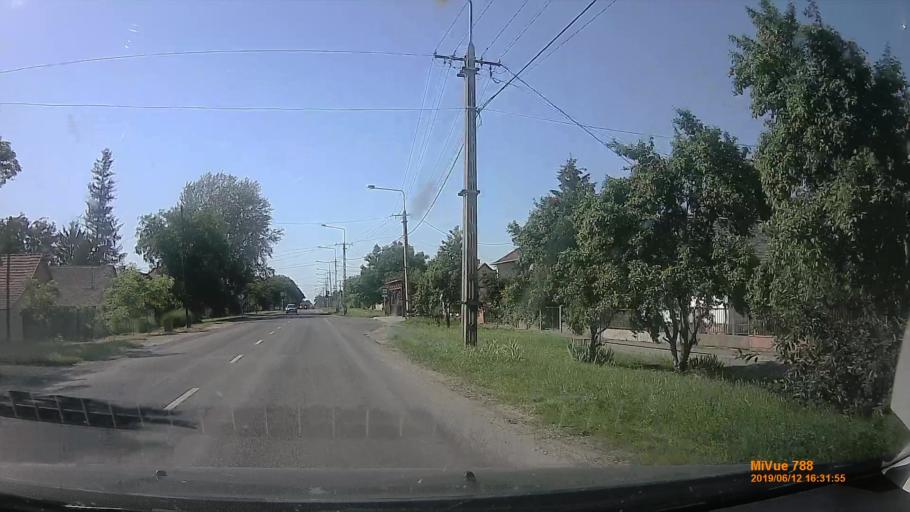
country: HU
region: Csongrad
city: Apatfalva
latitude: 46.1792
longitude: 20.5731
